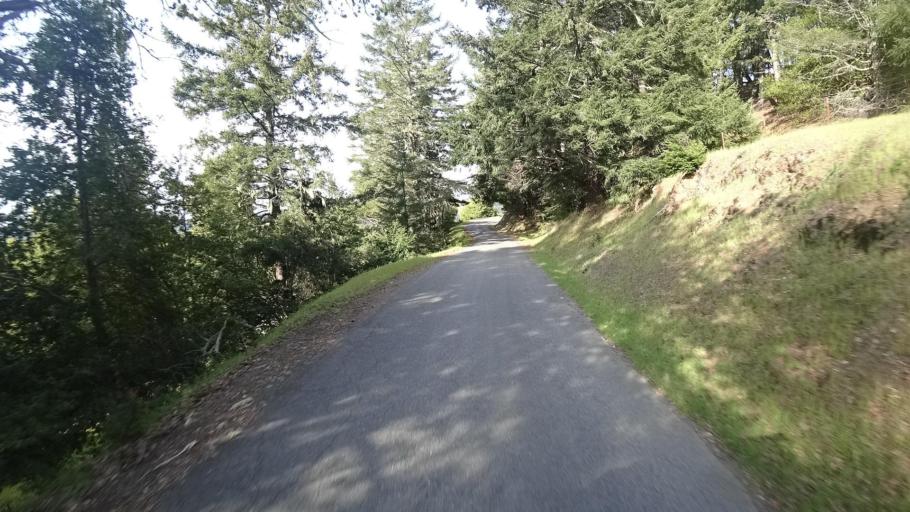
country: US
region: California
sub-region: Humboldt County
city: Hydesville
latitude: 40.6433
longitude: -123.9081
